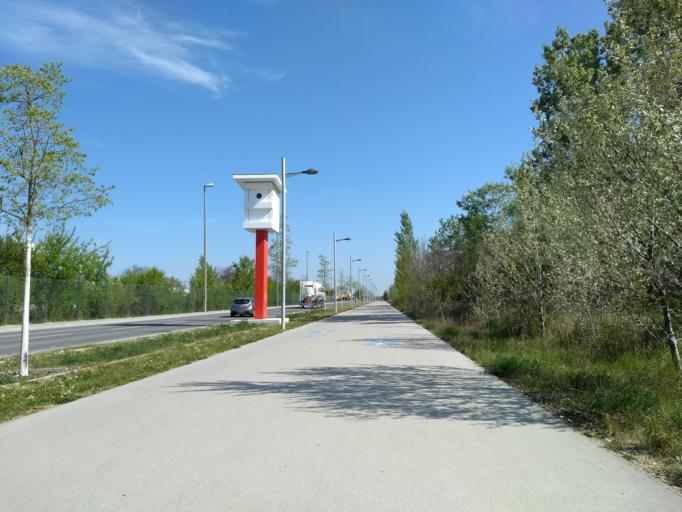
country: AT
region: Lower Austria
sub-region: Politischer Bezirk Ganserndorf
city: Gross-Enzersdorf
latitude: 48.2184
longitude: 16.5114
